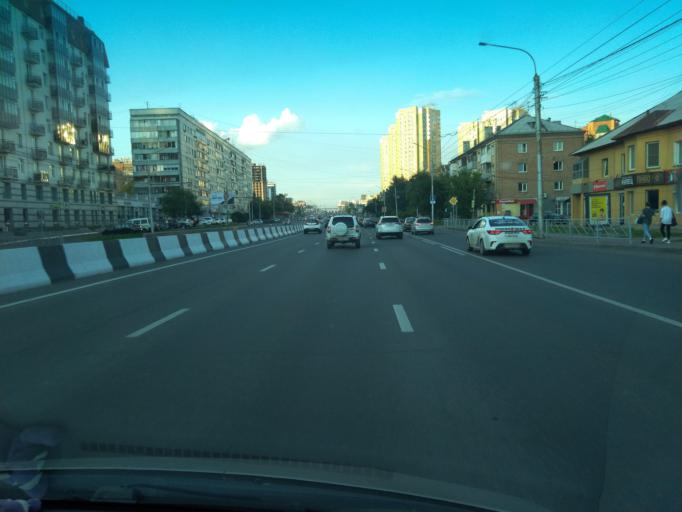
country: RU
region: Krasnoyarskiy
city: Krasnoyarsk
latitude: 56.0304
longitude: 92.9174
